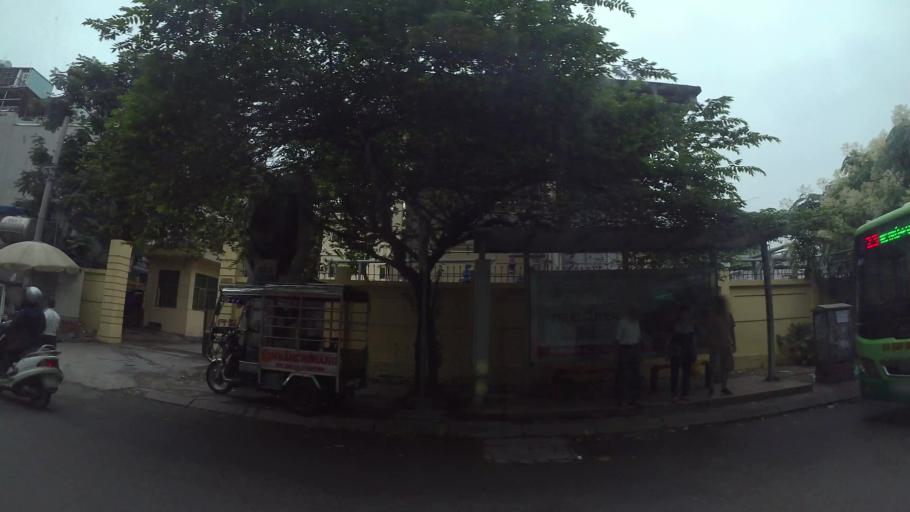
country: VN
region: Ha Noi
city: Dong Da
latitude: 21.0060
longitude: 105.8332
